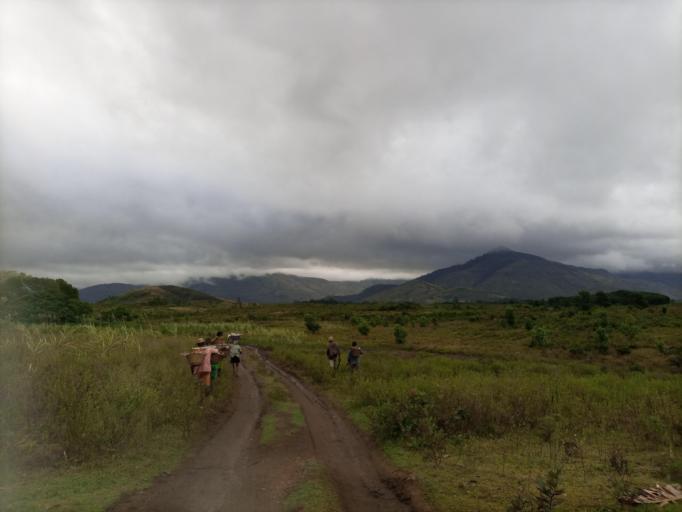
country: MG
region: Anosy
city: Fort Dauphin
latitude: -24.7602
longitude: 47.0697
